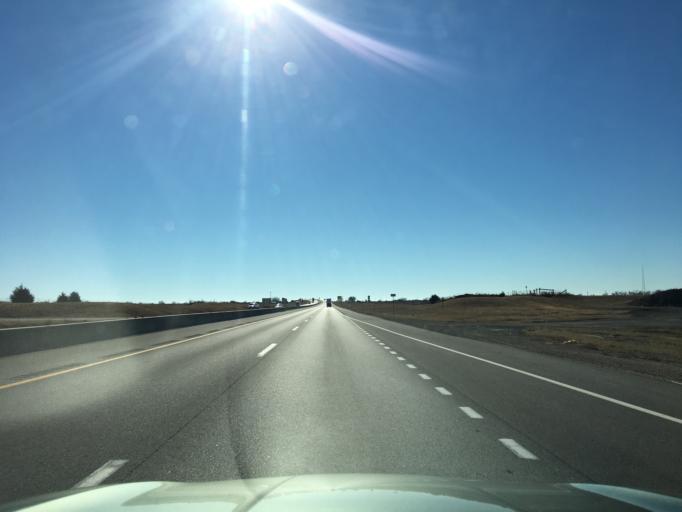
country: US
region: Kansas
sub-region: Sumner County
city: Wellington
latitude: 37.2755
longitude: -97.3404
